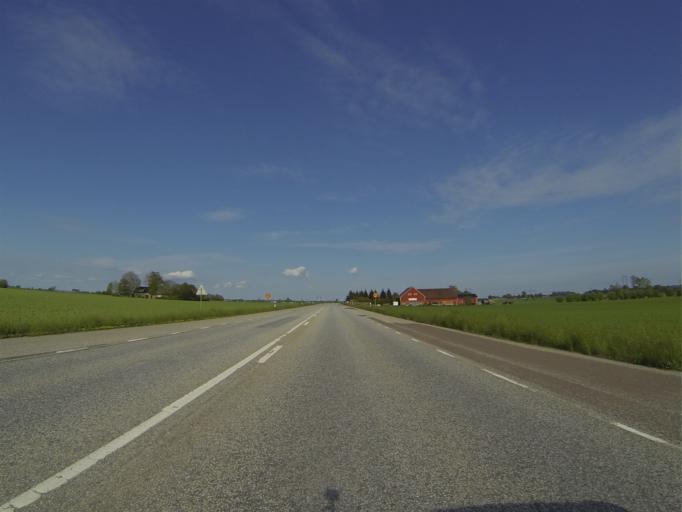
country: SE
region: Skane
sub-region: Staffanstorps Kommun
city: Hjaerup
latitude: 55.6419
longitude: 13.1516
